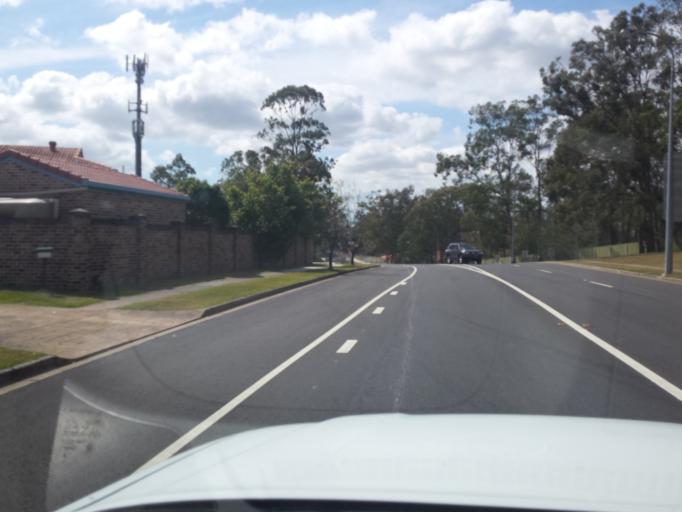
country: AU
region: Queensland
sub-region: Brisbane
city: Everton Park
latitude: -27.3870
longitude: 152.9866
